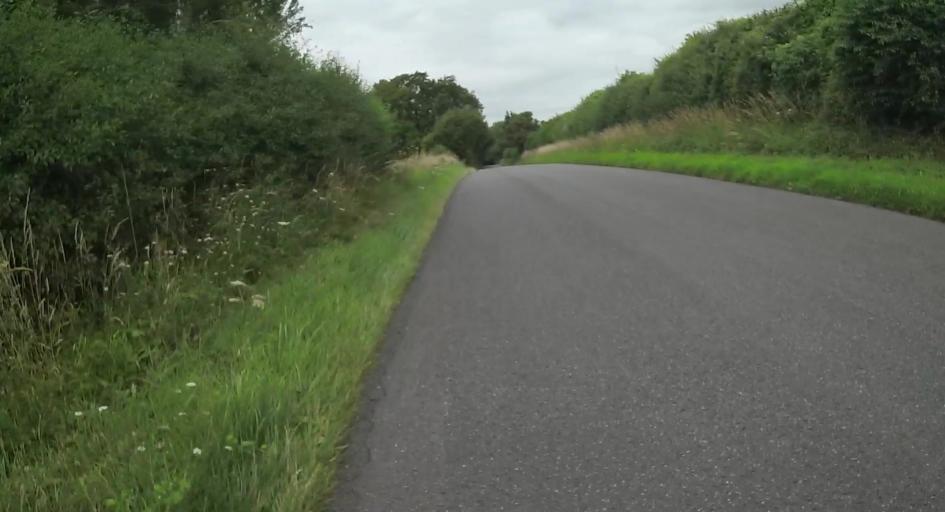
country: GB
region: England
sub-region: Hampshire
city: Bishops Waltham
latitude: 51.0212
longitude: -1.2004
